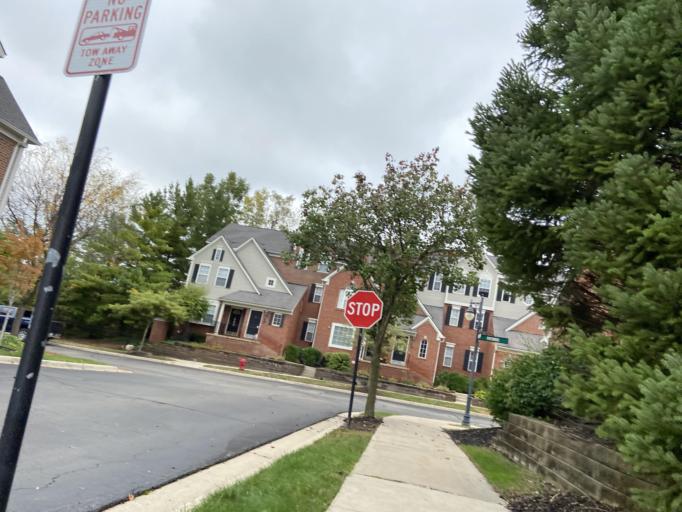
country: US
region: Michigan
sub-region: Oakland County
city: Novi
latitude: 42.4762
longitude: -83.4691
